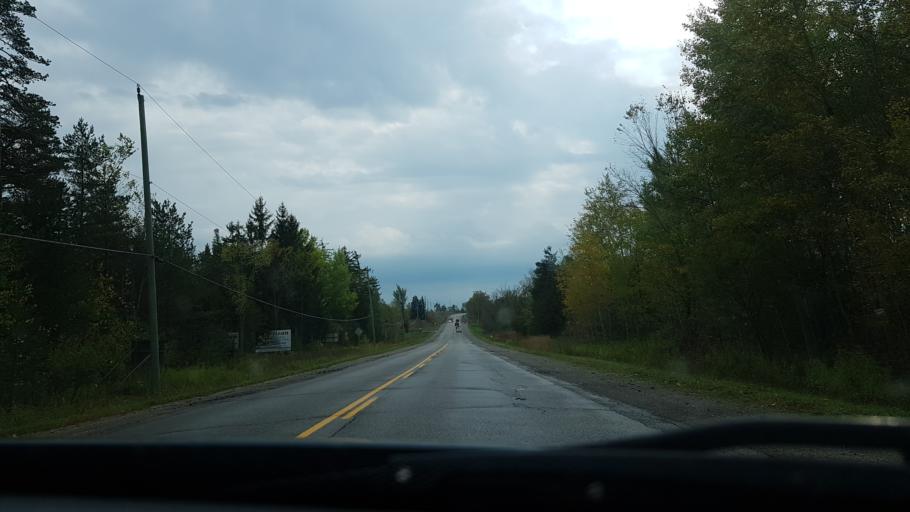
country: CA
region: Ontario
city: Omemee
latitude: 44.5091
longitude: -78.7420
